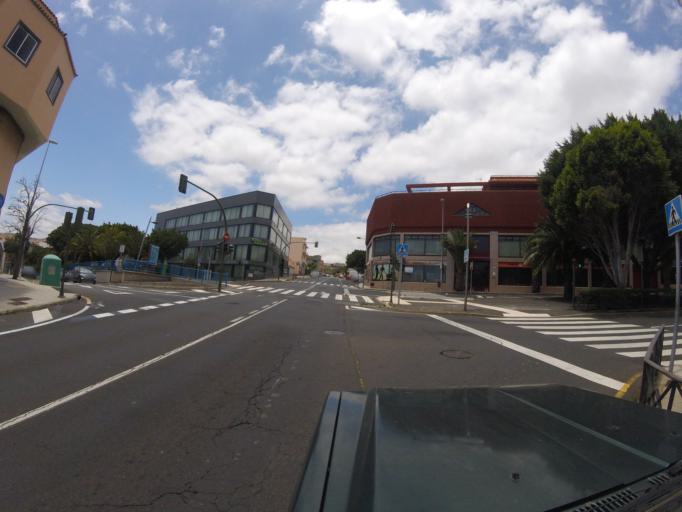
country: ES
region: Canary Islands
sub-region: Provincia de Santa Cruz de Tenerife
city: La Laguna
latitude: 28.4410
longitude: -16.3149
